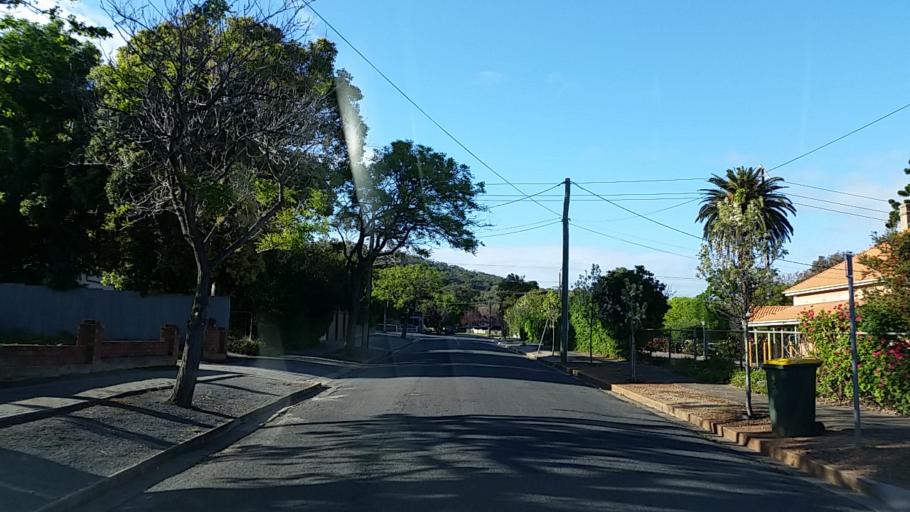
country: AU
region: South Australia
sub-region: Mitcham
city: Clapham
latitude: -34.9894
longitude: 138.6037
